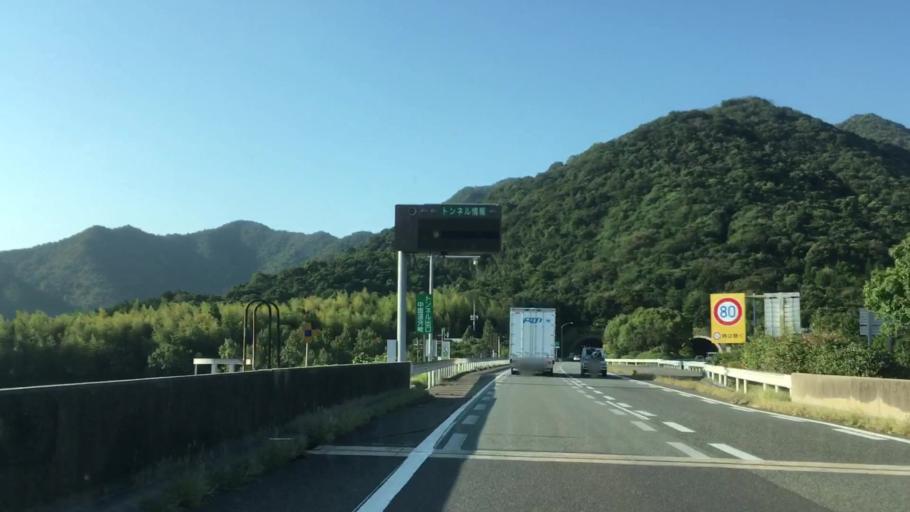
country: JP
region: Yamaguchi
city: Ogori-shimogo
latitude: 34.0984
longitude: 131.4518
